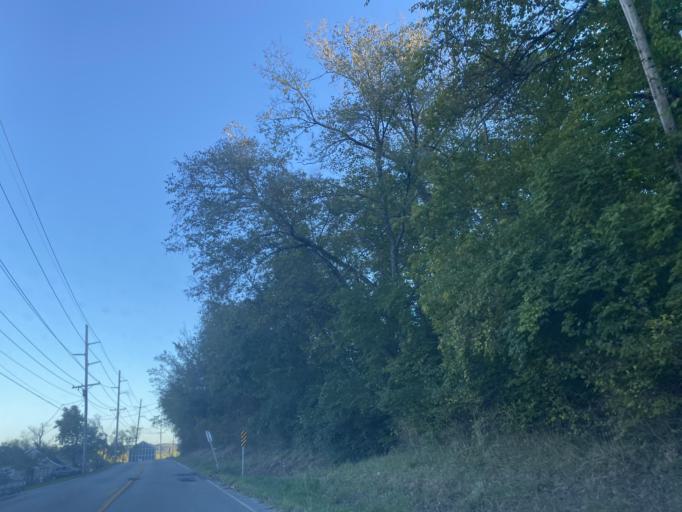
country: US
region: Kentucky
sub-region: Campbell County
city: Dayton
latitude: 39.1112
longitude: -84.4513
